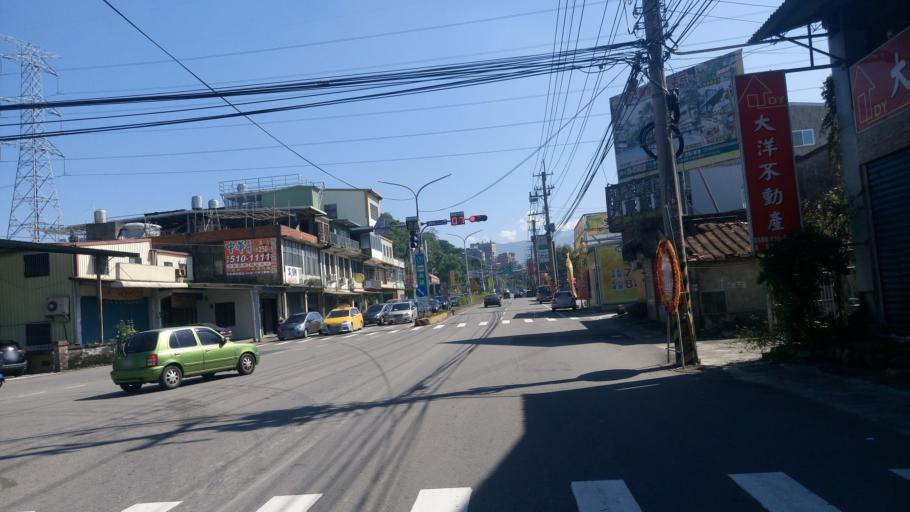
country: TW
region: Taiwan
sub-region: Hsinchu
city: Zhubei
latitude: 24.7263
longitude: 121.1292
